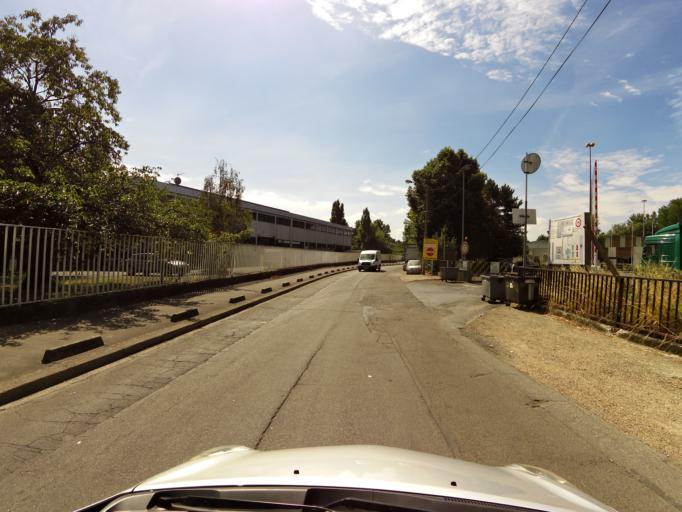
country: FR
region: Ile-de-France
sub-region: Departement de Seine-et-Marne
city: Chelles
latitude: 48.8701
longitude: 2.5958
